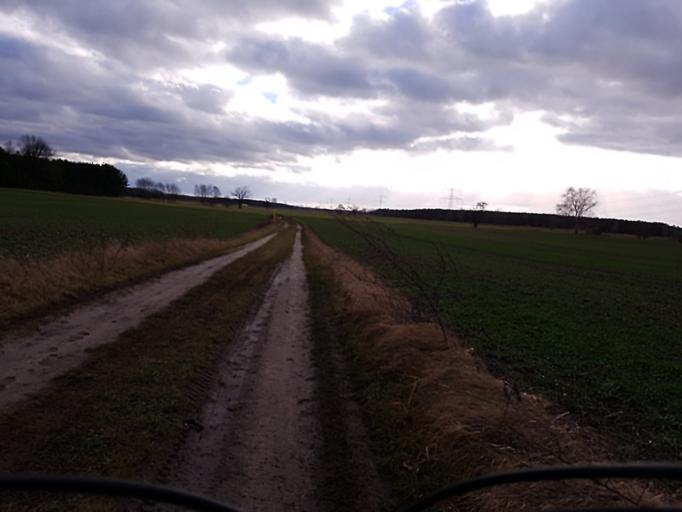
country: DE
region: Brandenburg
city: Schilda
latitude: 51.5844
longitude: 13.3823
